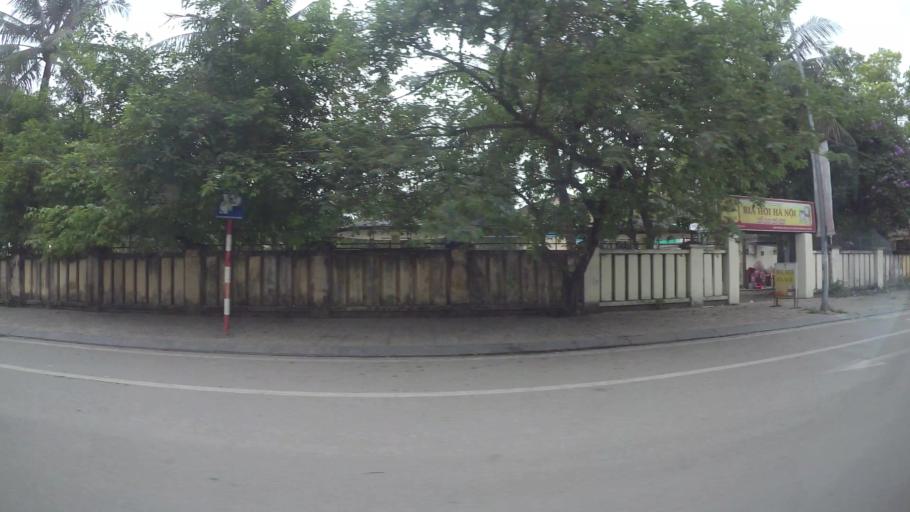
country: VN
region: Ha Noi
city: Tay Ho
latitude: 21.0583
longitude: 105.8220
